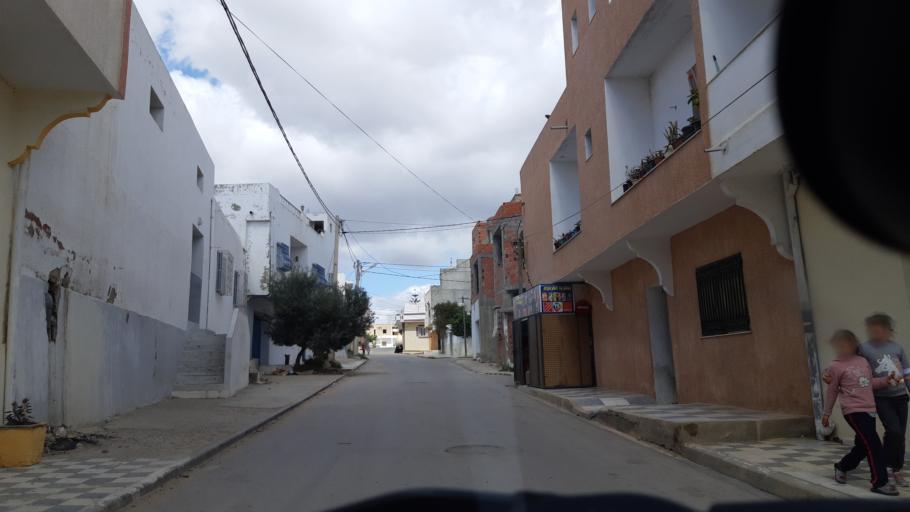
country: TN
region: Susah
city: Akouda
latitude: 35.8793
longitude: 10.5386
